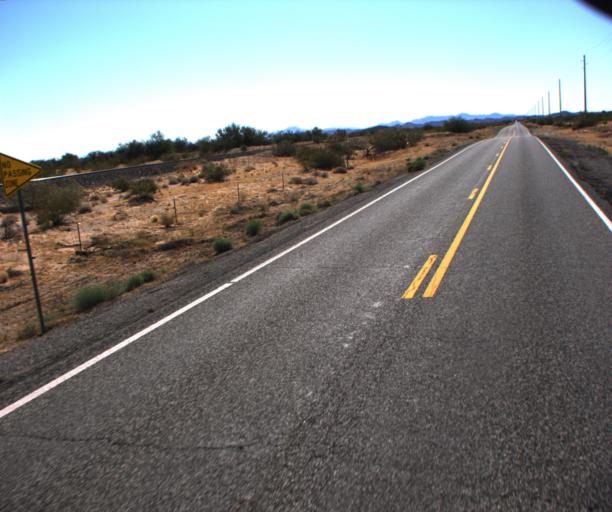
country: US
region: Arizona
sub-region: La Paz County
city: Cienega Springs
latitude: 33.9857
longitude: -114.0692
